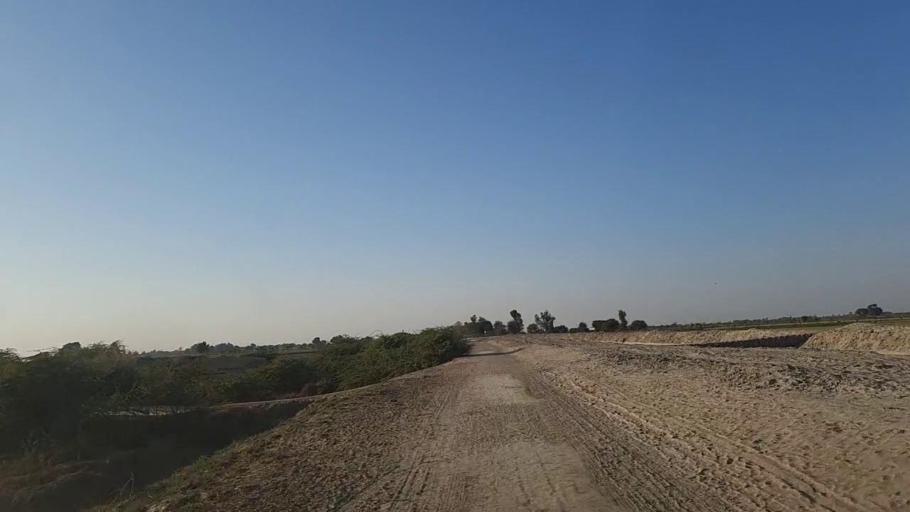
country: PK
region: Sindh
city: Naukot
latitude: 25.0011
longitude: 69.3970
